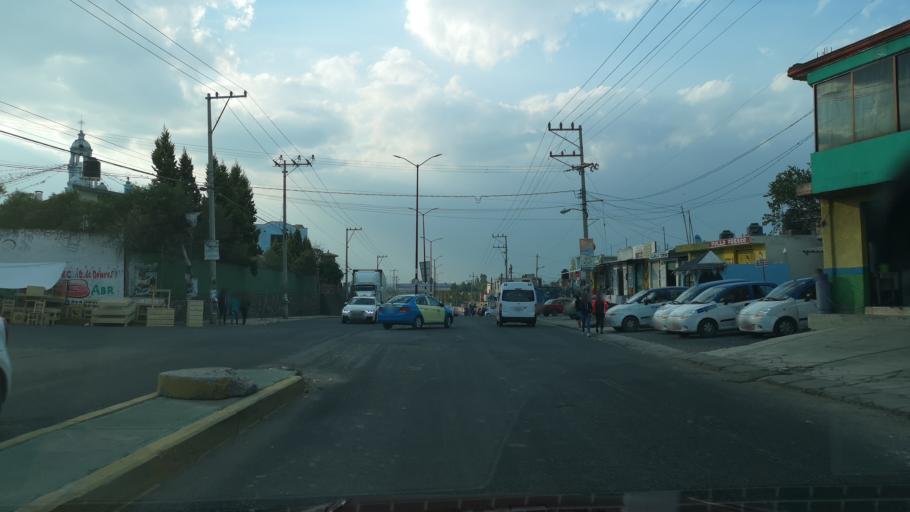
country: MX
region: Puebla
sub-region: Juan C. Bonilla
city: Santa Maria Zacatepec
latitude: 19.1218
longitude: -98.3643
